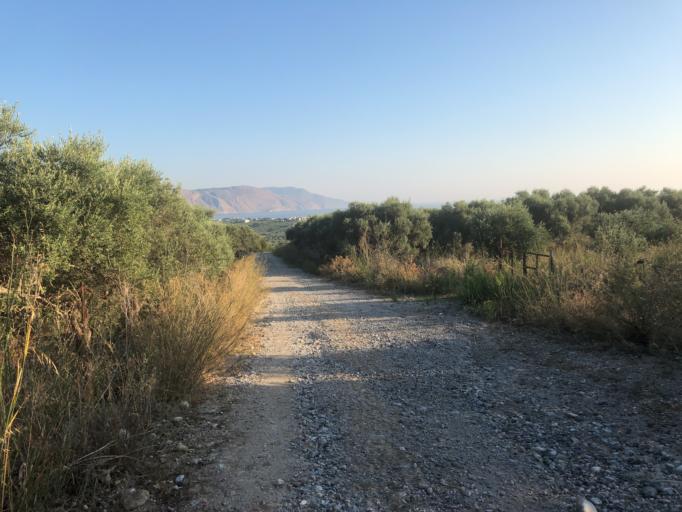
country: GR
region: Crete
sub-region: Nomos Chanias
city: Georgioupolis
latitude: 35.3358
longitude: 24.2907
